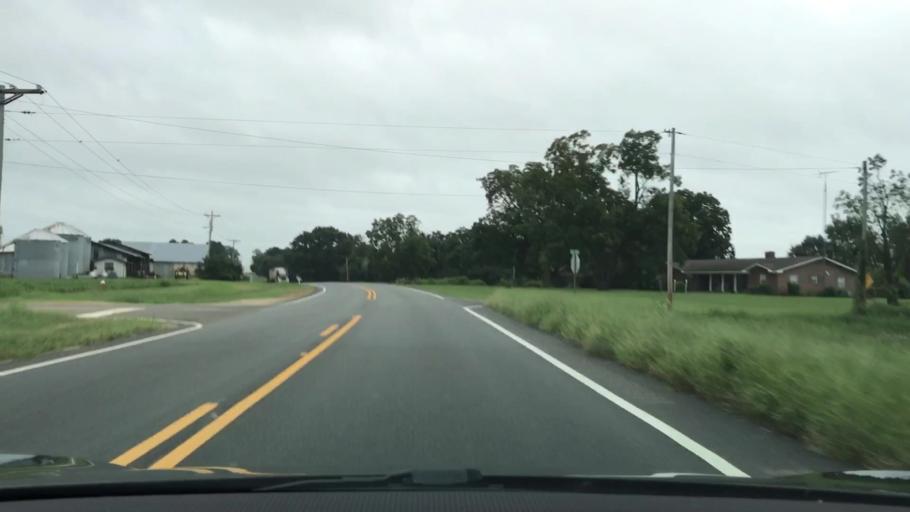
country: US
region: Alabama
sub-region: Covington County
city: Opp
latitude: 31.2728
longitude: -86.1589
